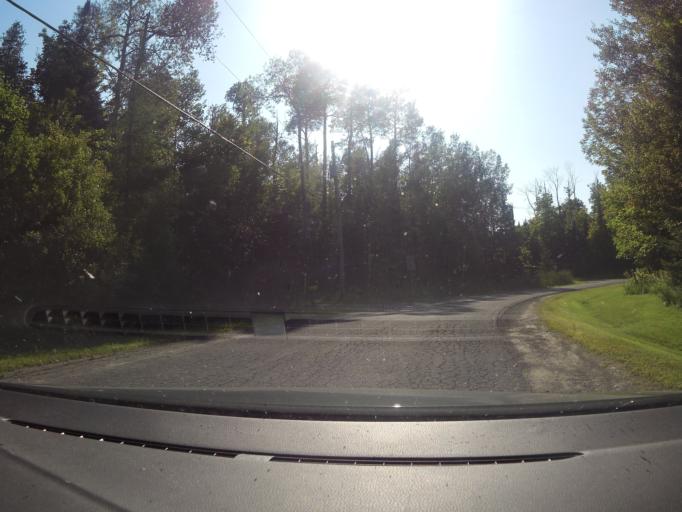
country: CA
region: Ontario
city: Carleton Place
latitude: 45.2951
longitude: -76.0634
